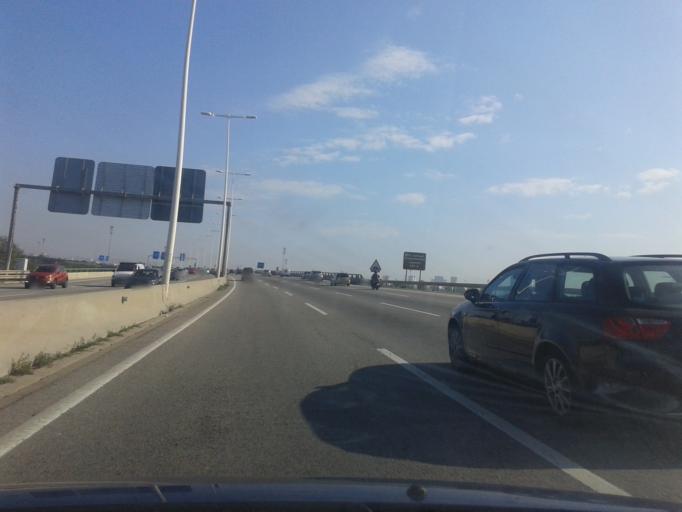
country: ES
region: Catalonia
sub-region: Provincia de Barcelona
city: Cornella de Llobregat
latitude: 41.3393
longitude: 2.0874
